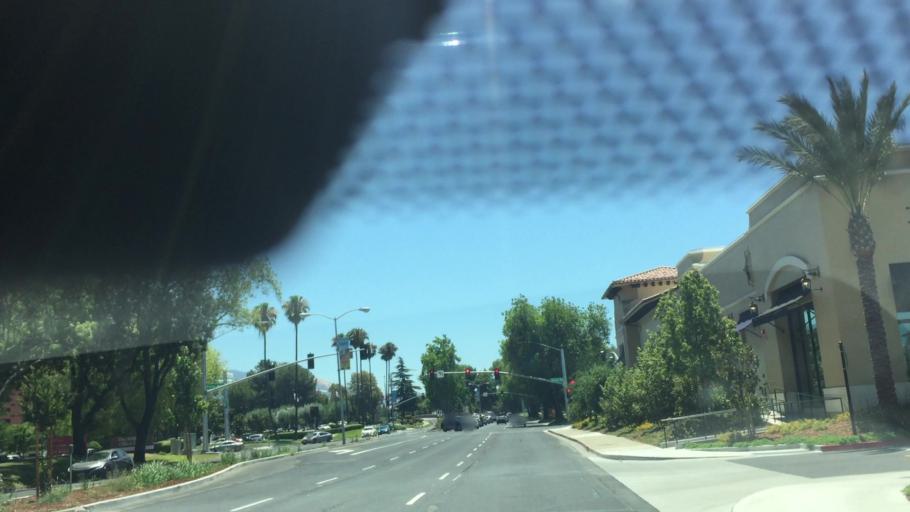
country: US
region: California
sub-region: Contra Costa County
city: Pacheco
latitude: 37.9722
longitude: -122.0566
